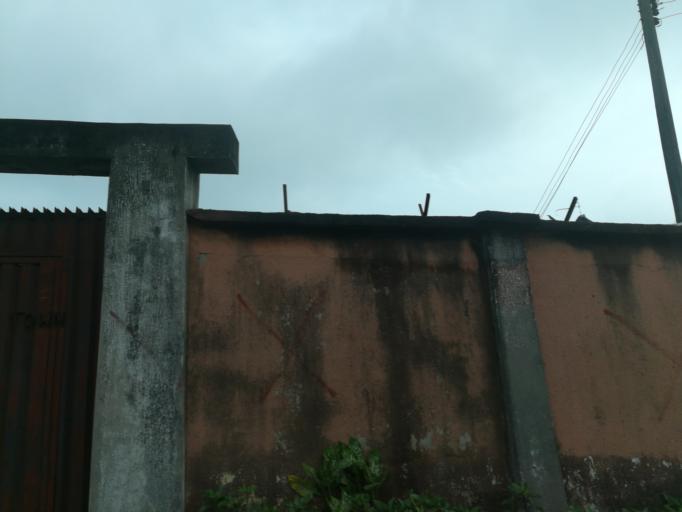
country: NG
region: Rivers
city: Port Harcourt
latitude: 4.8761
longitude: 6.9867
